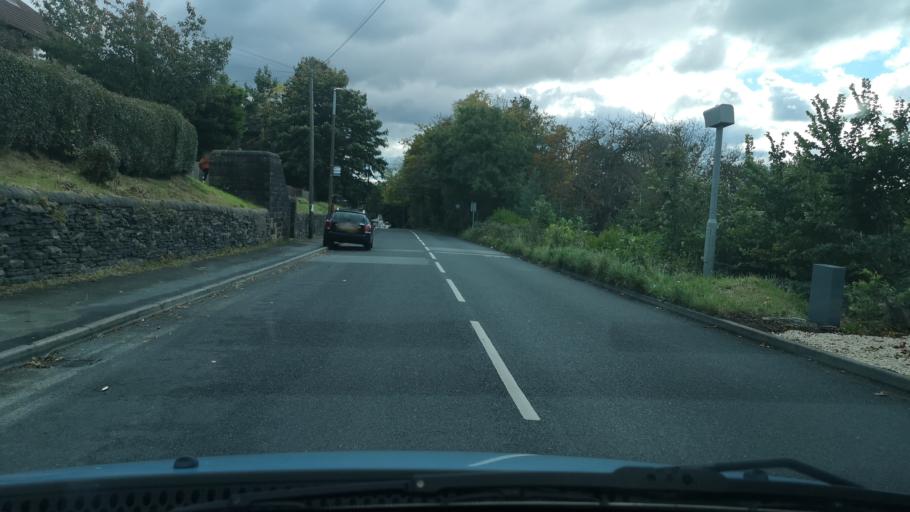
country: GB
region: England
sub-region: Kirklees
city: Heckmondwike
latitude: 53.6987
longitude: -1.6608
